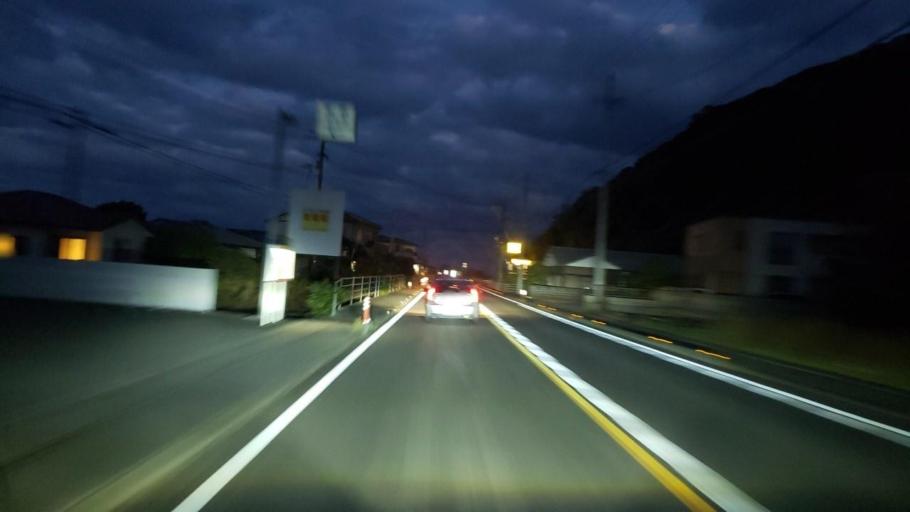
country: JP
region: Tokushima
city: Narutocho-mitsuishi
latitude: 34.2198
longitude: 134.4890
